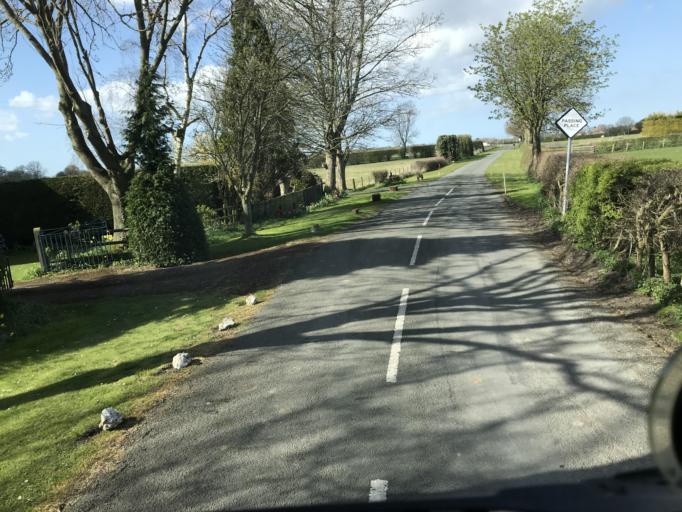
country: GB
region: England
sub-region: Cheshire West and Chester
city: Blacon
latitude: 53.1713
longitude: -2.9473
